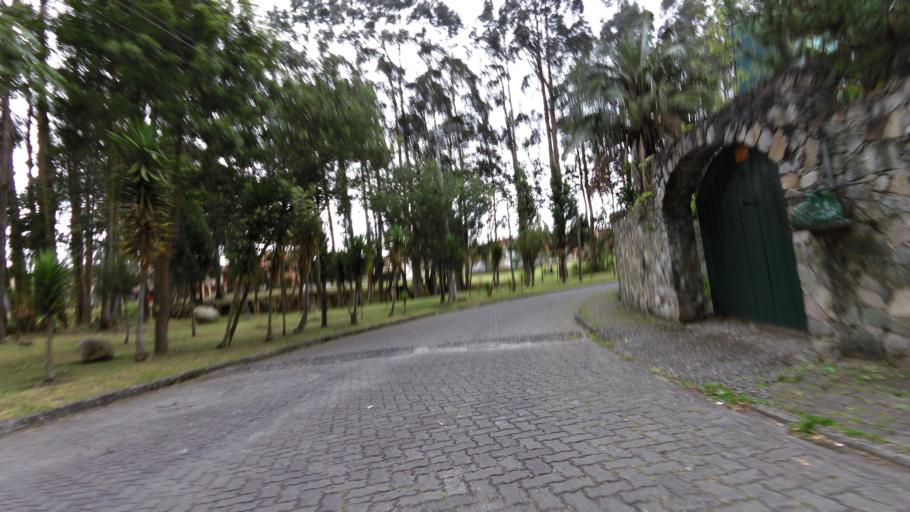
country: EC
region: Azuay
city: Cuenca
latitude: -2.9183
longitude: -79.0220
